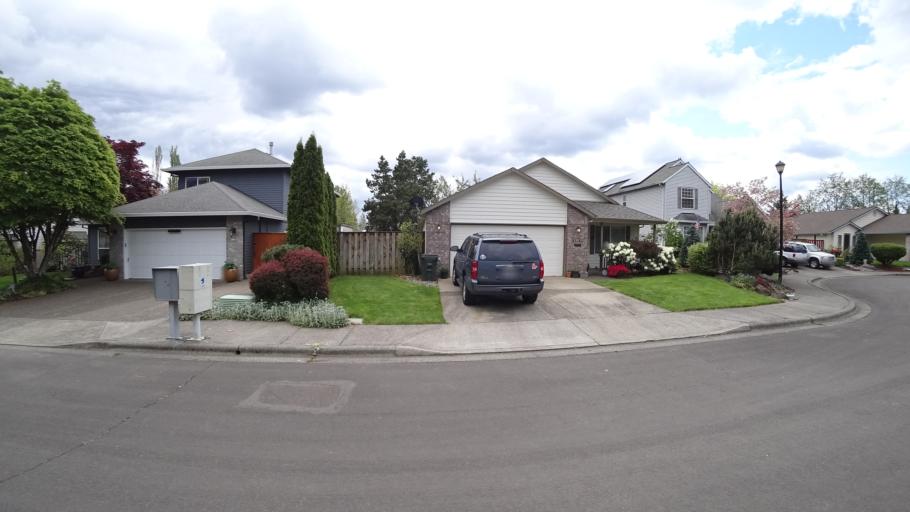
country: US
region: Oregon
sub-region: Washington County
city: Rockcreek
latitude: 45.5593
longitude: -122.8967
